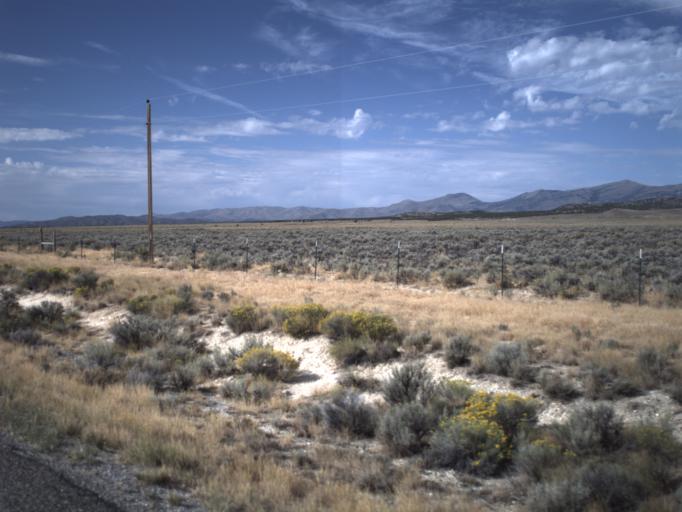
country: US
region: Idaho
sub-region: Cassia County
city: Burley
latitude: 41.7536
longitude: -113.5149
